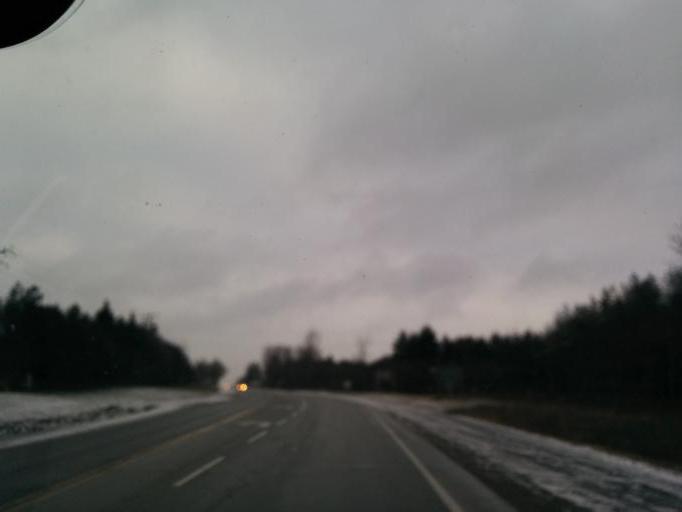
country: CA
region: Ontario
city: Orangeville
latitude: 43.8556
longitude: -80.0011
